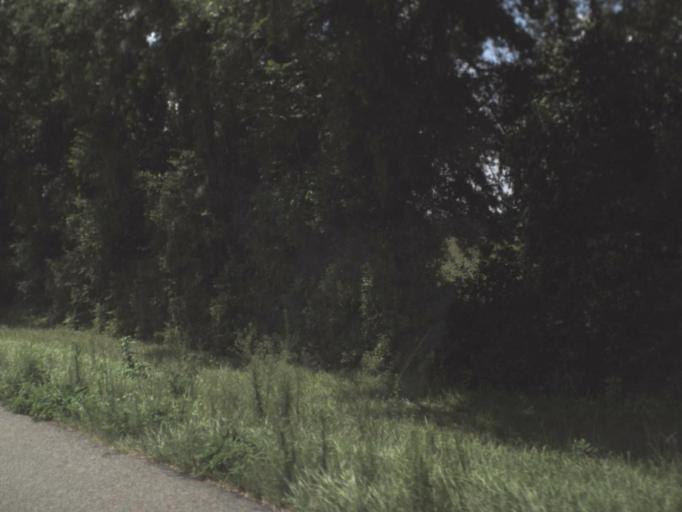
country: US
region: Florida
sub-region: Gilchrist County
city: Trenton
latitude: 29.6565
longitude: -82.8432
